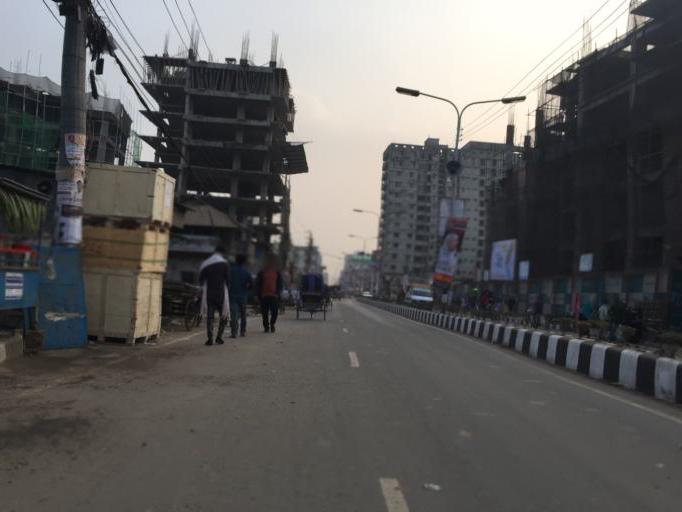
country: BD
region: Dhaka
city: Azimpur
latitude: 23.7960
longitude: 90.3491
